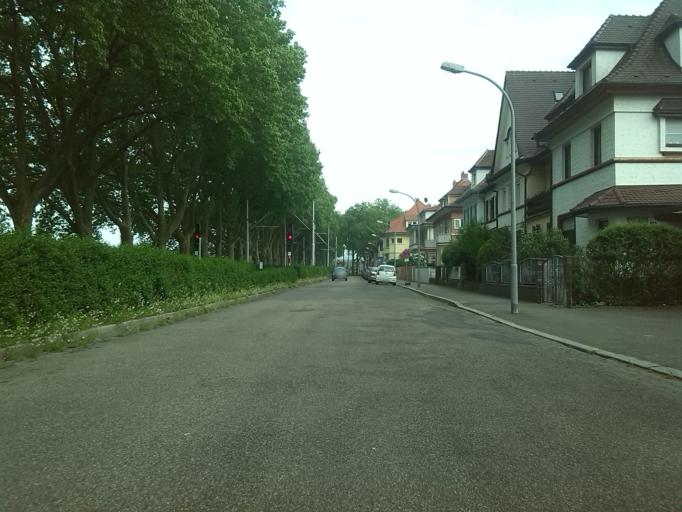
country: DE
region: Baden-Wuerttemberg
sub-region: Karlsruhe Region
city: Mannheim
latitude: 49.4794
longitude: 8.5180
